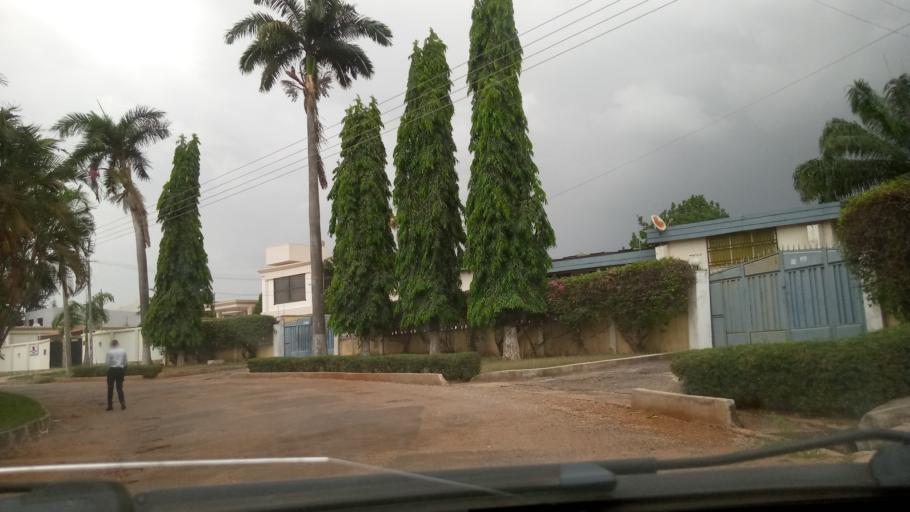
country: GH
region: Greater Accra
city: Dome
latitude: 5.6145
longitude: -0.2073
